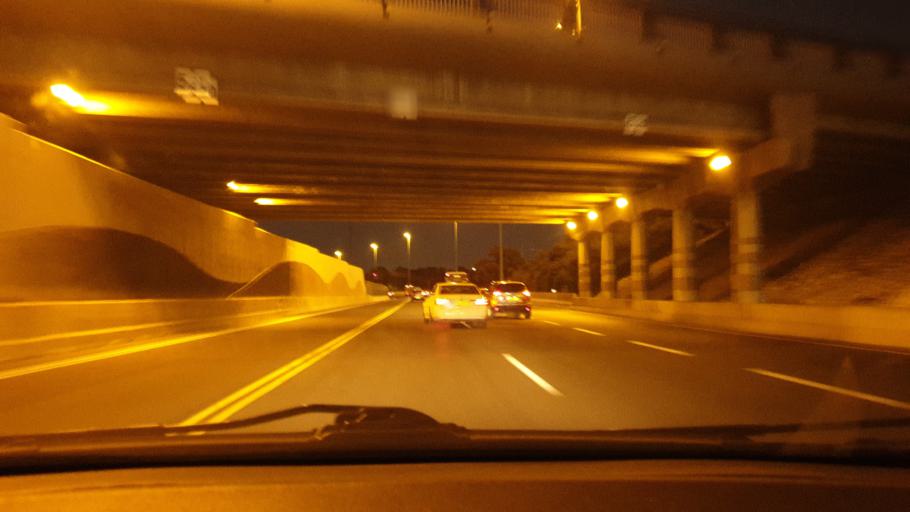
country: IL
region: Tel Aviv
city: Bat Yam
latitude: 32.0366
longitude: 34.7688
